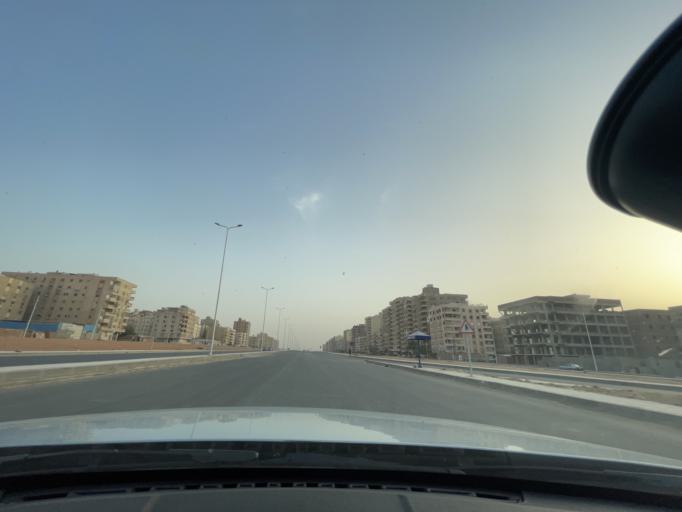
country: EG
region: Muhafazat al Qahirah
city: Cairo
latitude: 30.0557
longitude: 31.3733
